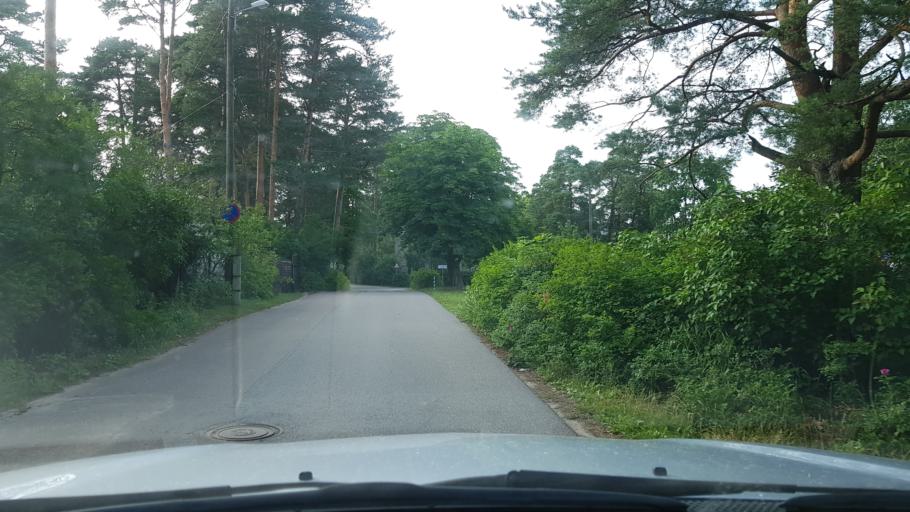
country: EE
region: Ida-Virumaa
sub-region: Narva-Joesuu linn
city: Narva-Joesuu
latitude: 59.4591
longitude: 28.0439
